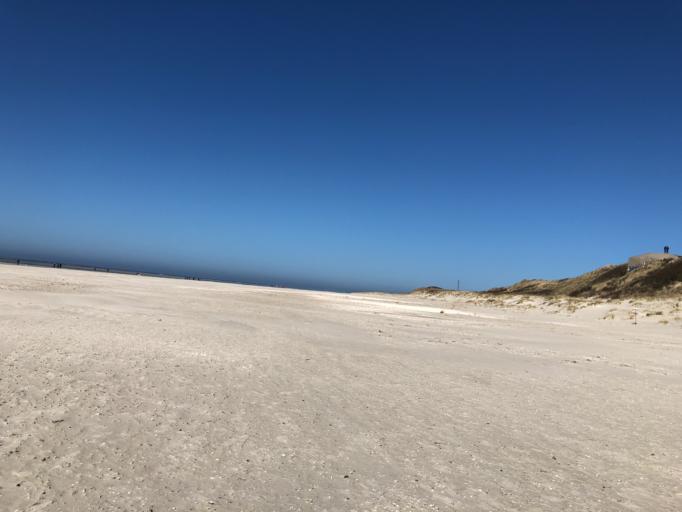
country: DK
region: South Denmark
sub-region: Varde Kommune
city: Oksbol
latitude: 55.5552
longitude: 8.0842
